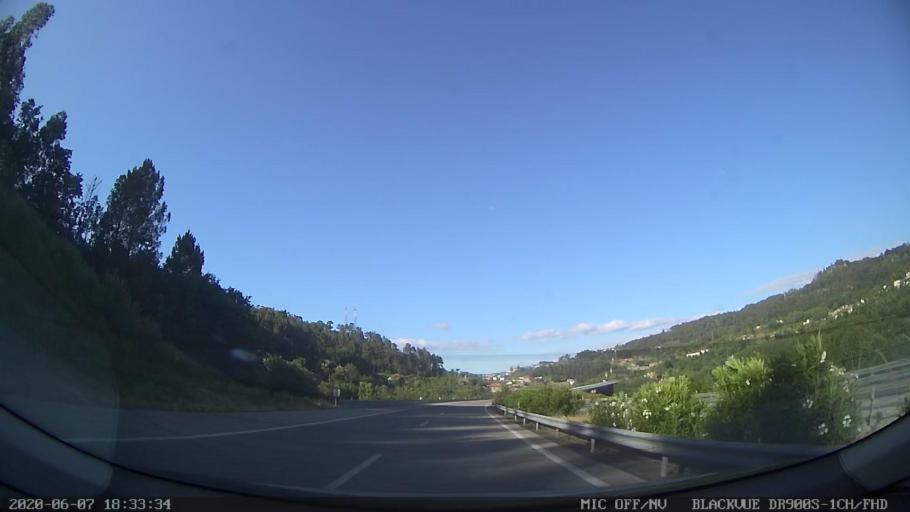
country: PT
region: Braga
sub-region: Guimaraes
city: Serzedo
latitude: 41.4226
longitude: -8.1968
